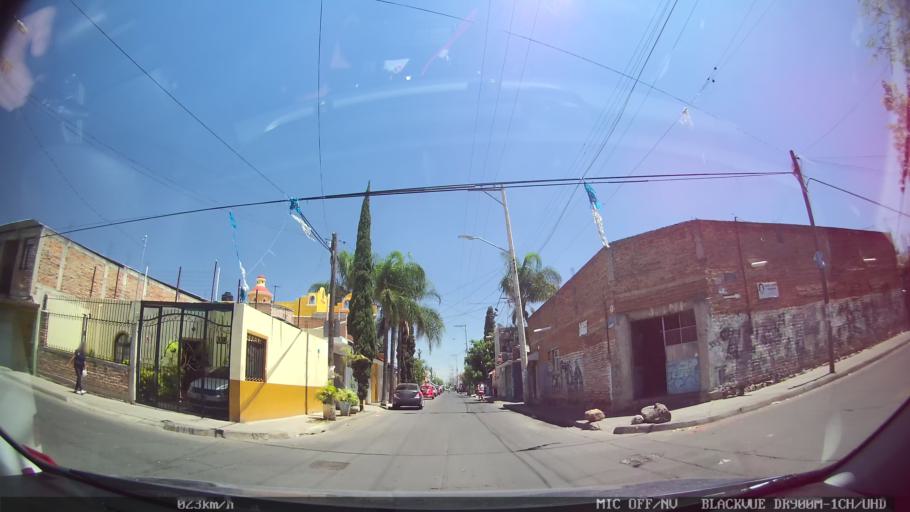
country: MX
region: Jalisco
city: Tlaquepaque
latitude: 20.6634
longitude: -103.2753
